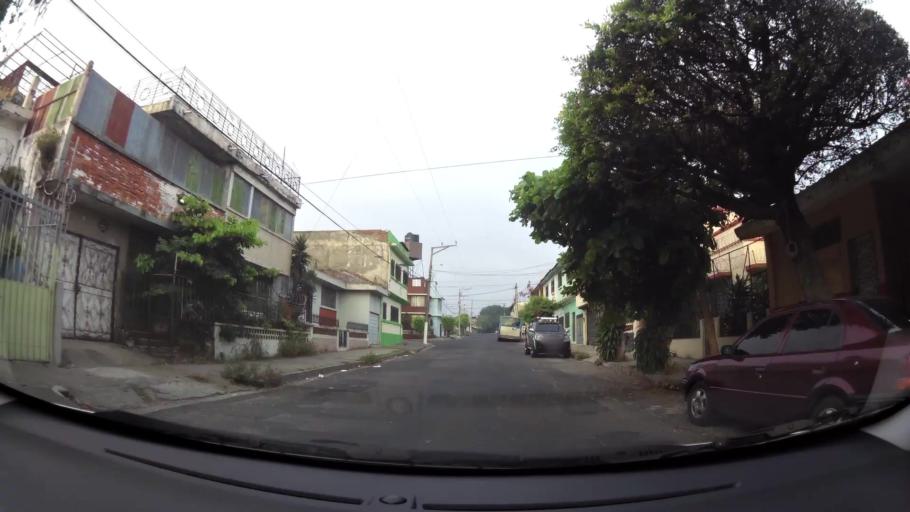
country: SV
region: San Salvador
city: San Salvador
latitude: 13.7060
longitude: -89.1882
